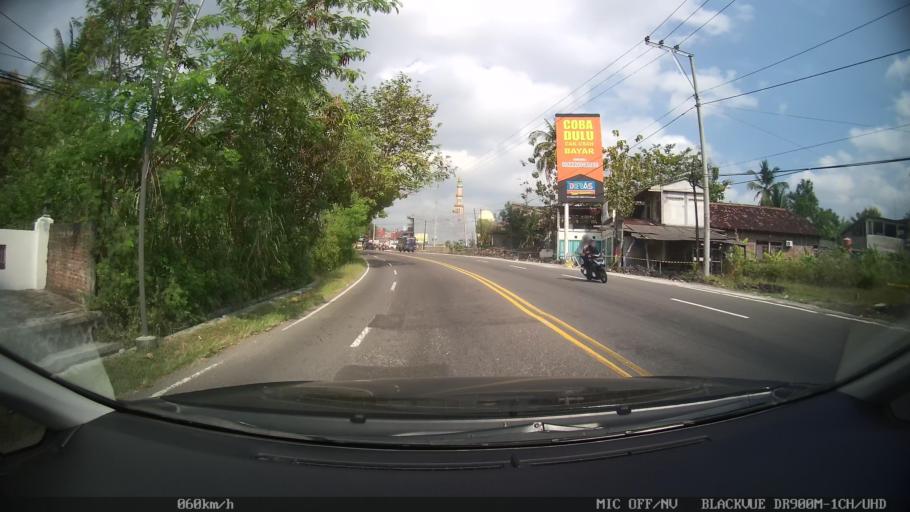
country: ID
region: Daerah Istimewa Yogyakarta
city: Srandakan
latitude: -7.8661
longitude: 110.1698
